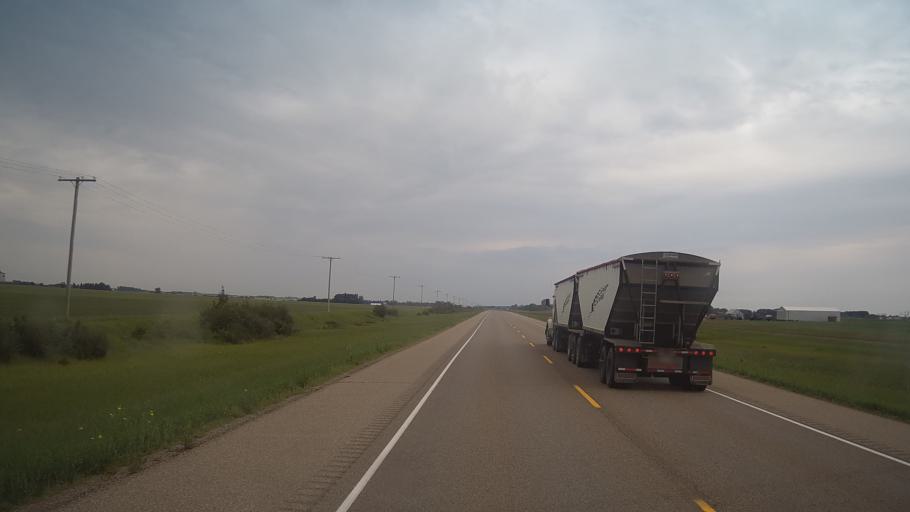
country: CA
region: Saskatchewan
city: Langham
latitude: 52.1289
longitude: -107.1959
